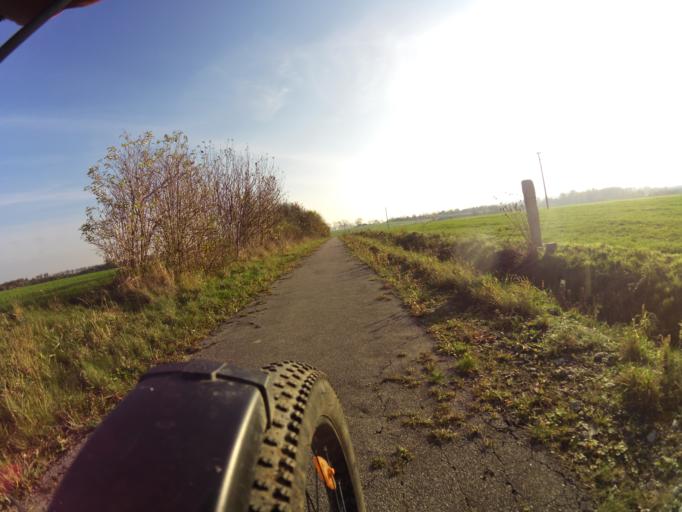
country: PL
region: Pomeranian Voivodeship
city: Strzelno
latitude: 54.7643
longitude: 18.2528
